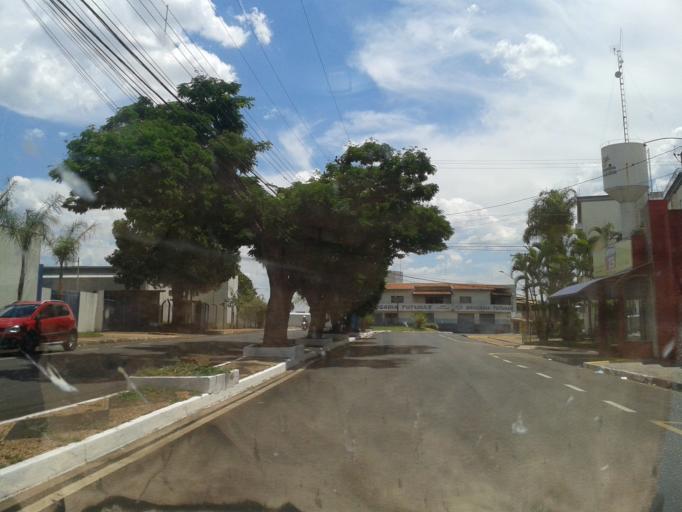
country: BR
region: Minas Gerais
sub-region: Uberaba
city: Uberaba
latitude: -19.7409
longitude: -47.9589
